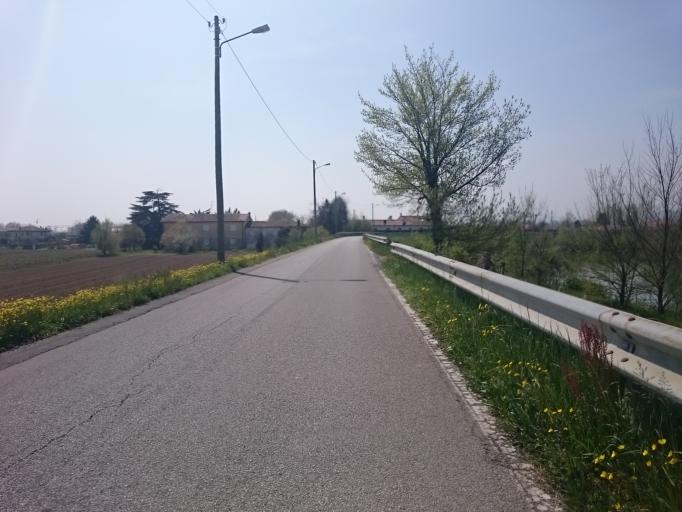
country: IT
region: Veneto
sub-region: Provincia di Padova
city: Tencarola
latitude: 45.3856
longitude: 11.8126
